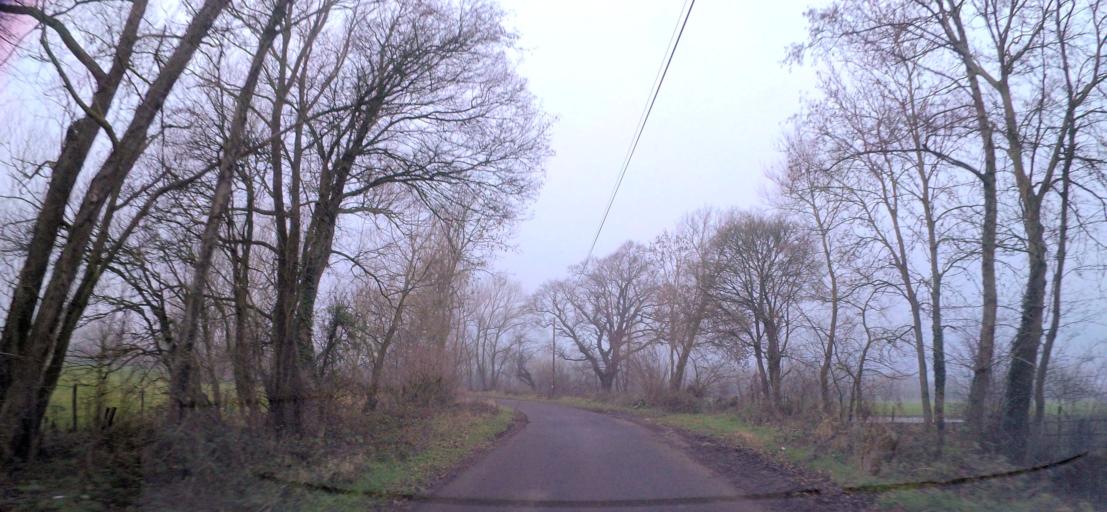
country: GB
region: England
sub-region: West Berkshire
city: Theale
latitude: 51.4110
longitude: -1.1061
